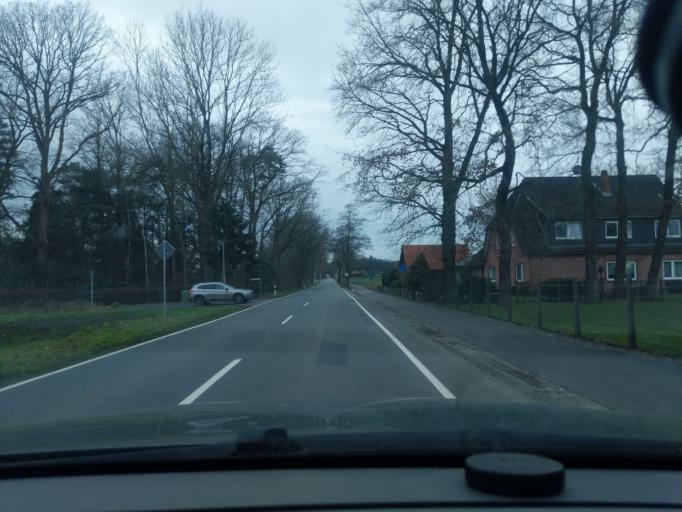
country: DE
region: Lower Saxony
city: Lauenbruck
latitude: 53.1520
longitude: 9.5393
